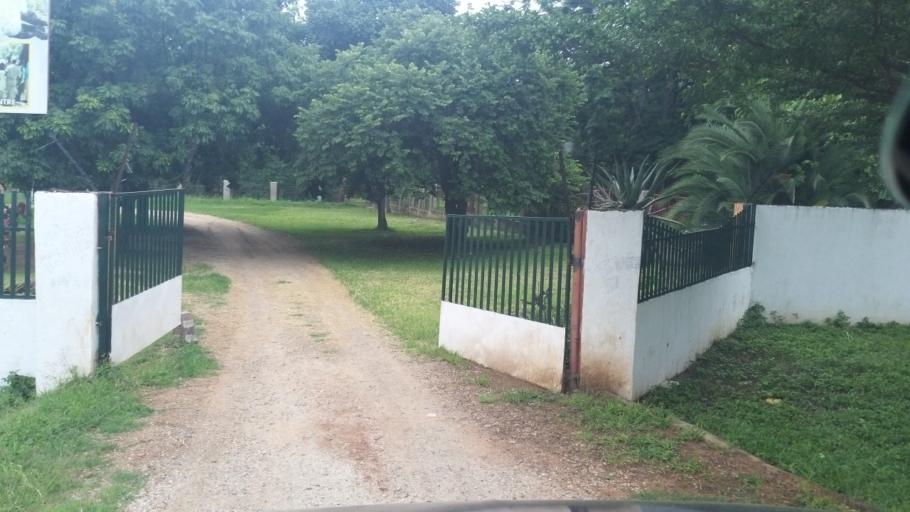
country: ZM
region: Lusaka
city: Lusaka
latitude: -15.5615
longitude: 28.2733
